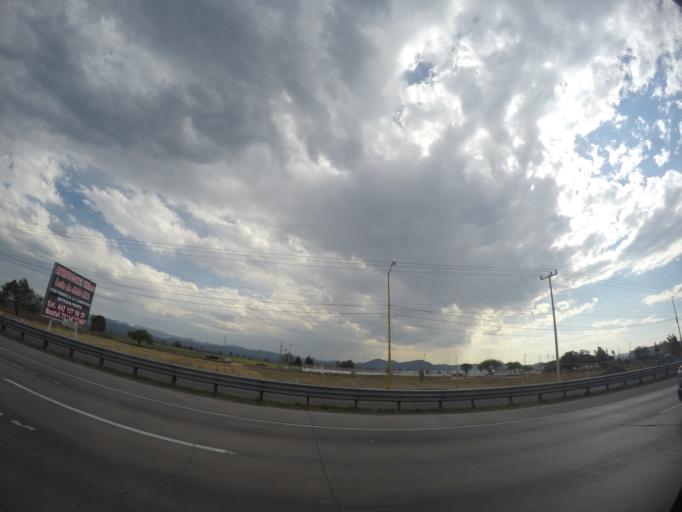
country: MX
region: Queretaro
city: La Estancia
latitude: 20.4283
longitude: -100.0579
